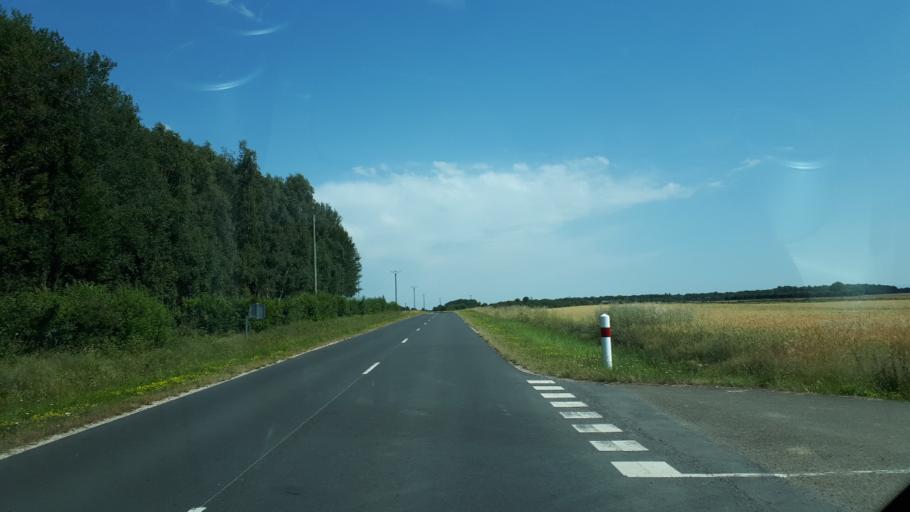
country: FR
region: Centre
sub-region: Departement du Loir-et-Cher
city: Droue
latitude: 48.0000
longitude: 1.0410
